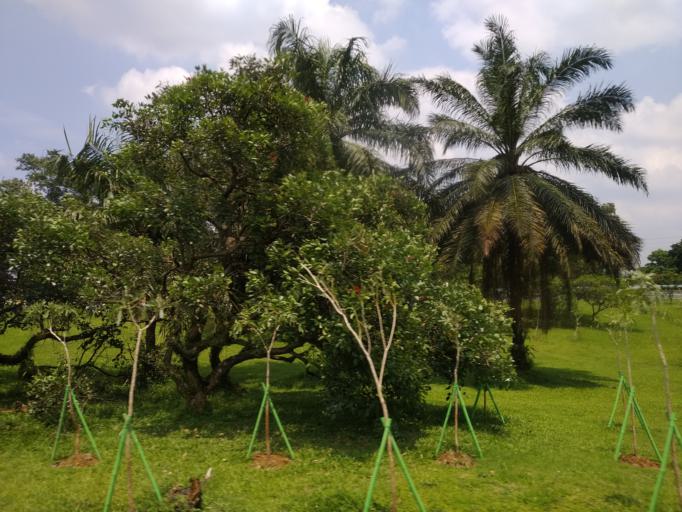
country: ID
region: West Java
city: Bogor
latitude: -6.5962
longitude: 106.8301
